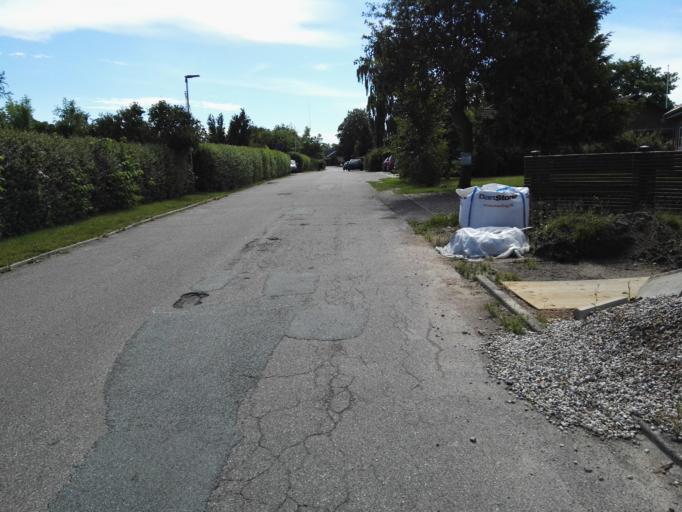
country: DK
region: Capital Region
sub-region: Egedal Kommune
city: Olstykke
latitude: 55.7964
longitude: 12.1530
